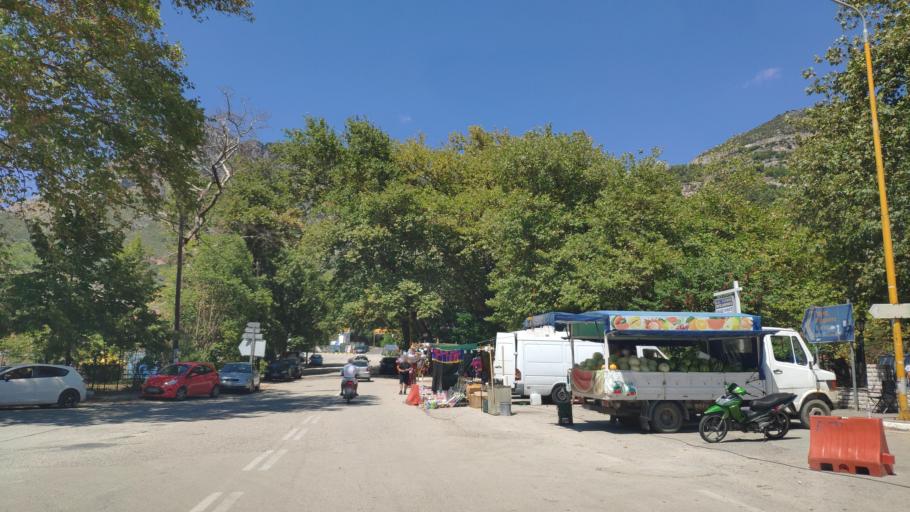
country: GR
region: Epirus
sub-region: Nomos Prevezis
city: Kanalaki
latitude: 39.3254
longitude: 20.6074
